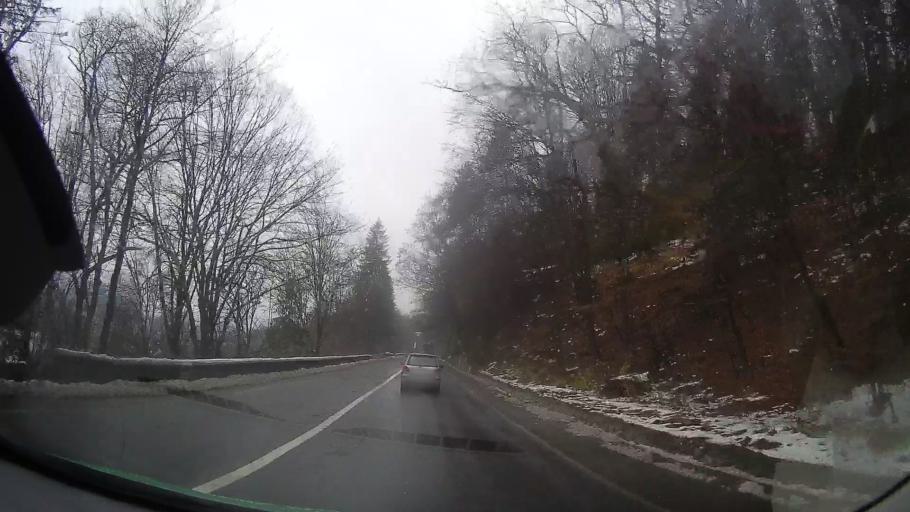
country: RO
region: Neamt
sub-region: Comuna Tarcau
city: Tarcau
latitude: 46.8993
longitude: 26.1193
